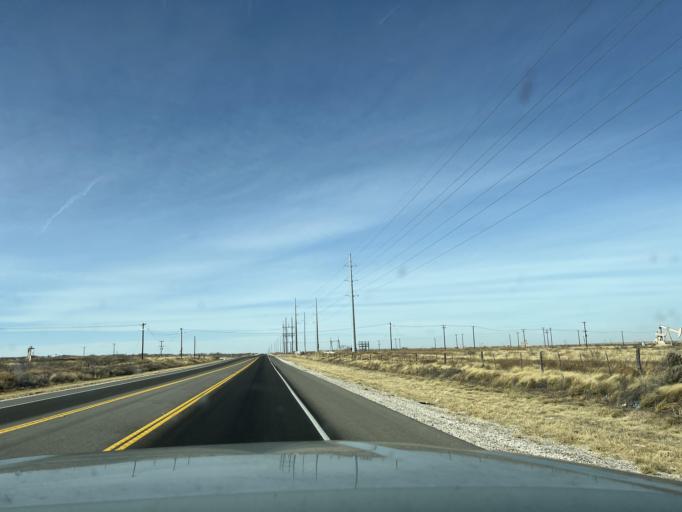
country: US
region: Texas
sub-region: Andrews County
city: Andrews
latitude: 32.3499
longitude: -102.7321
